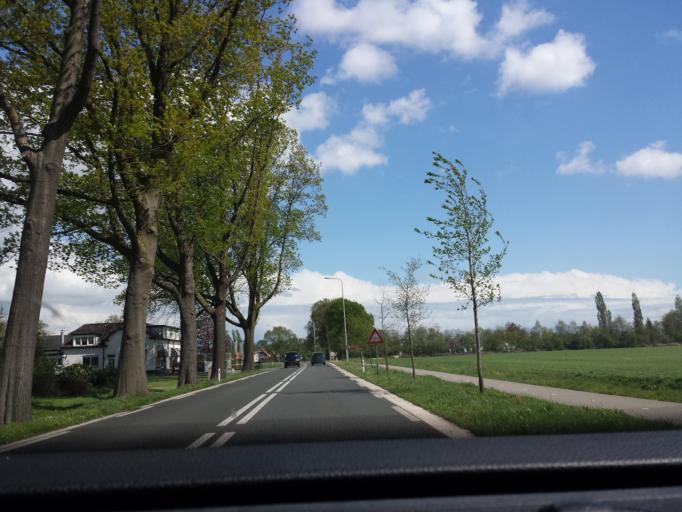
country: NL
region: Gelderland
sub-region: Gemeente Bronckhorst
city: Zelhem
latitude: 52.0279
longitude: 6.4023
